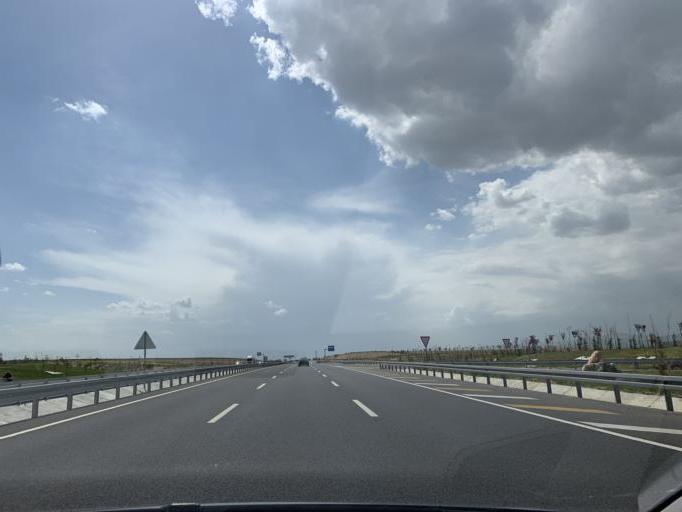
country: TR
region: Ankara
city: Temelli
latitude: 39.7431
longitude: 32.4101
